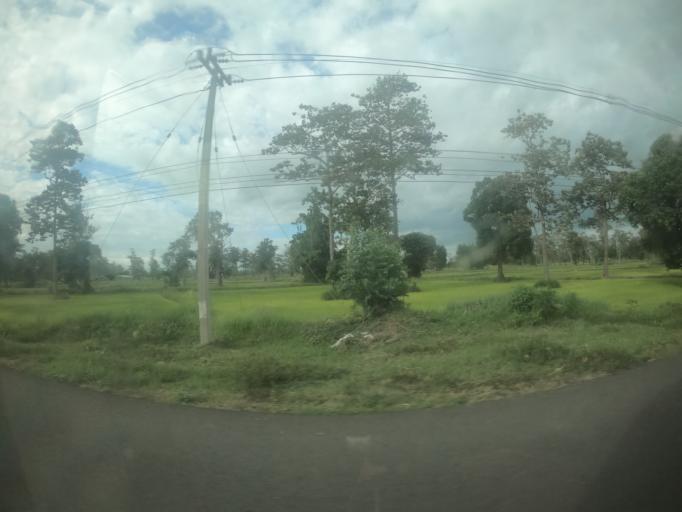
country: TH
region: Surin
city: Prasat
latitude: 14.5756
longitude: 103.4827
